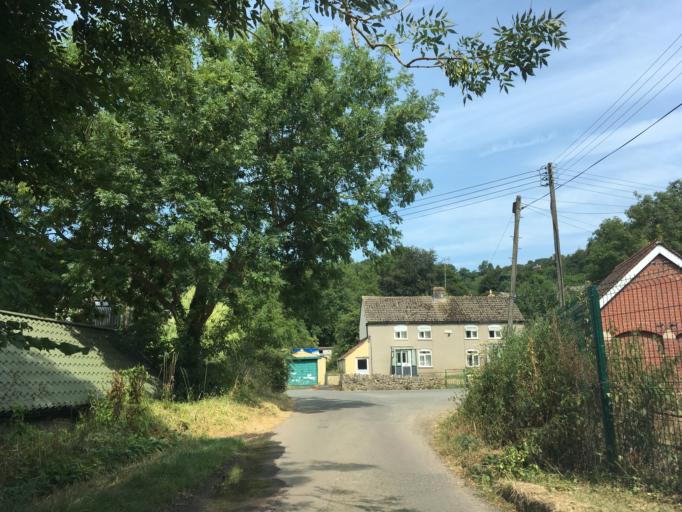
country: GB
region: England
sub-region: Gloucestershire
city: Wotton-under-Edge
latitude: 51.6427
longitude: -2.3374
